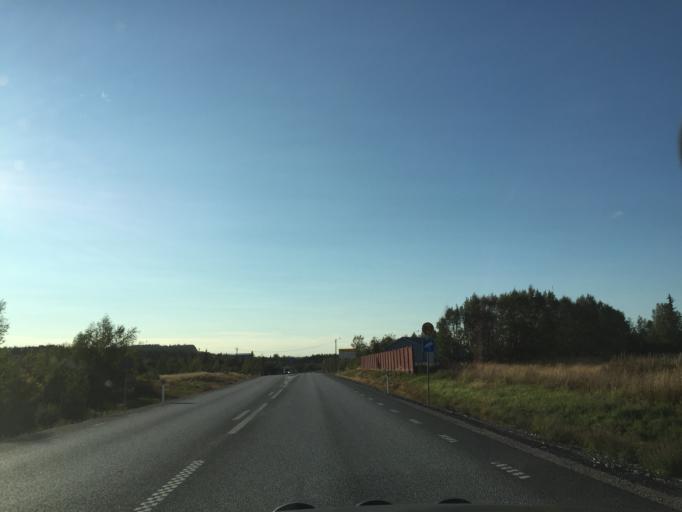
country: SE
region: Norrbotten
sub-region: Gallivare Kommun
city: Malmberget
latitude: 67.6449
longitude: 21.0445
